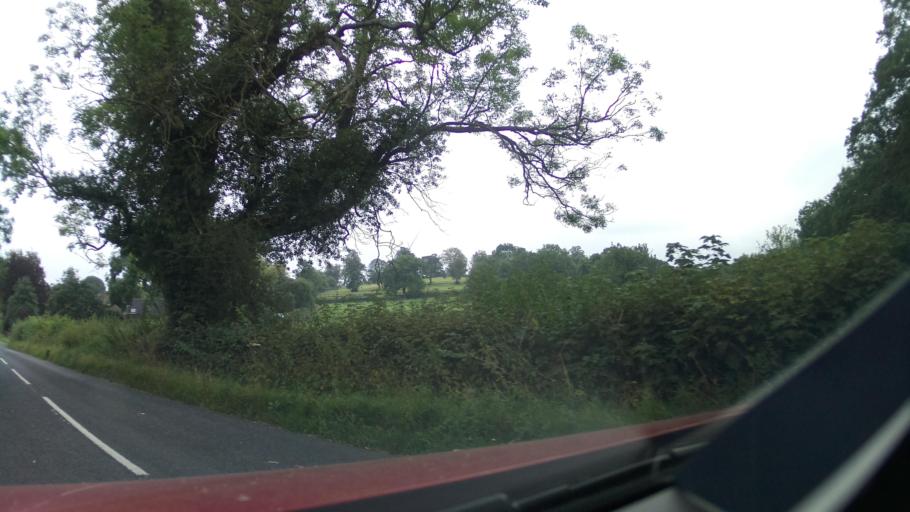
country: GB
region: England
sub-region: Derbyshire
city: Wirksworth
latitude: 53.0261
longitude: -1.5648
